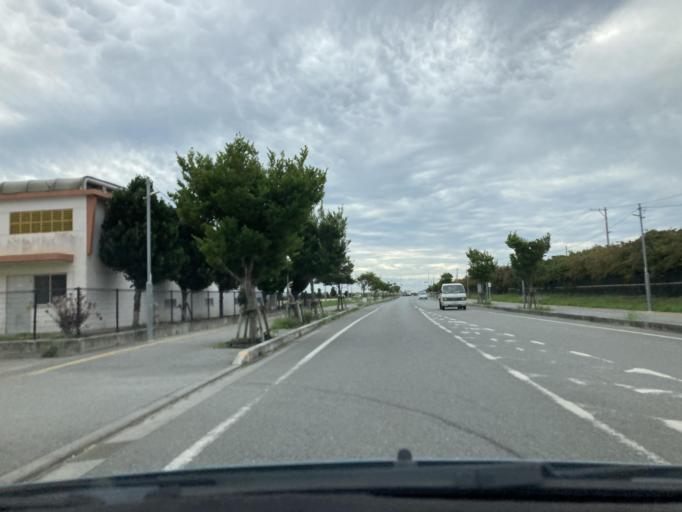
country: JP
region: Okinawa
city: Ishikawa
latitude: 26.3958
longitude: 127.7410
